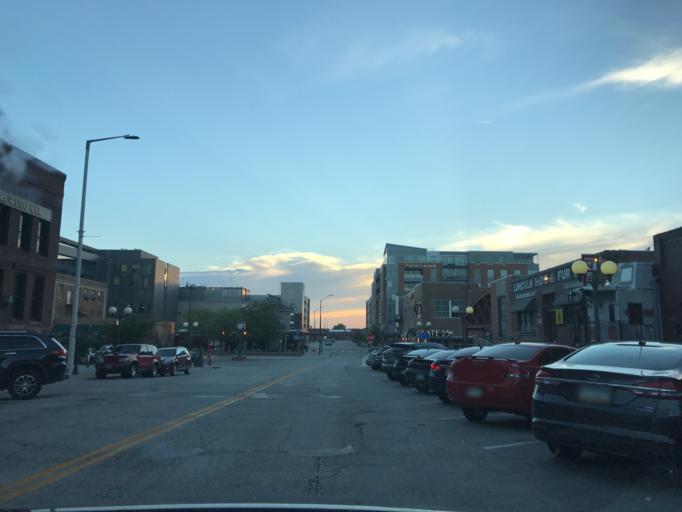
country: US
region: Nebraska
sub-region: Lancaster County
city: Lincoln
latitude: 40.8160
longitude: -96.7101
